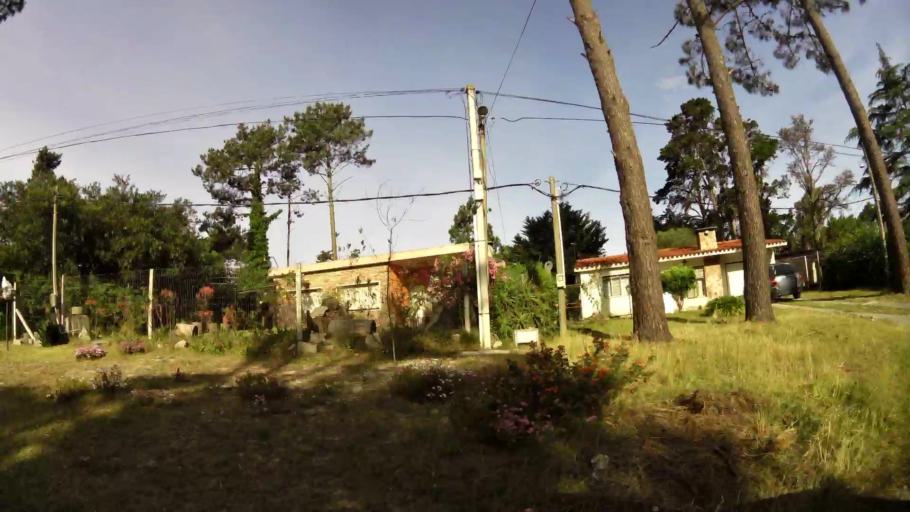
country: UY
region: Canelones
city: Empalme Olmos
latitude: -34.7813
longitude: -55.8541
